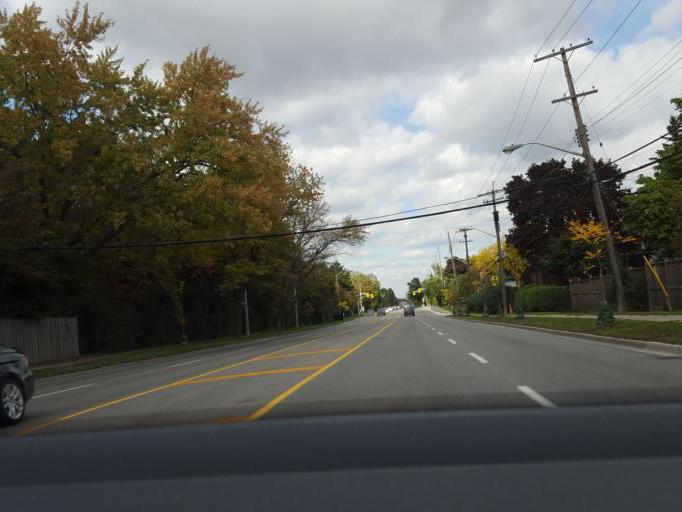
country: CA
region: Ontario
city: Willowdale
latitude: 43.7445
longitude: -79.3581
